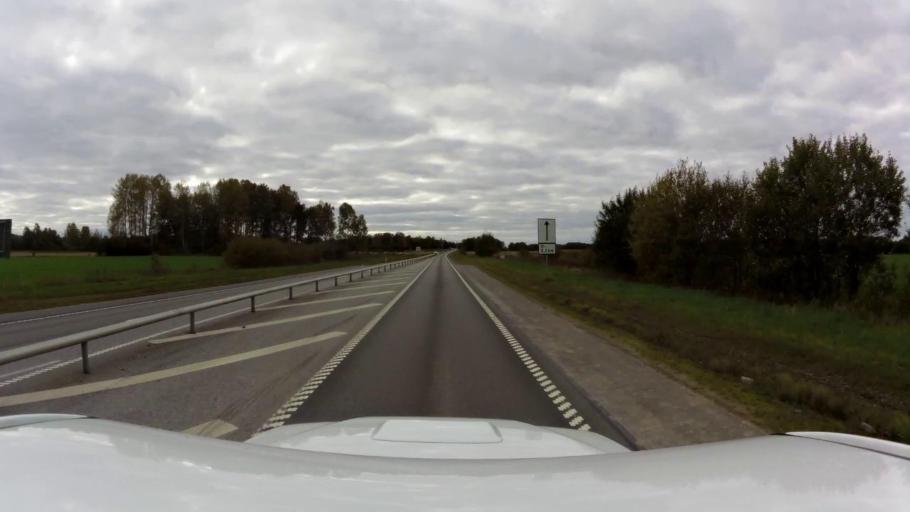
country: SE
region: OEstergoetland
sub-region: Linkopings Kommun
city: Malmslatt
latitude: 58.3705
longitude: 15.5438
